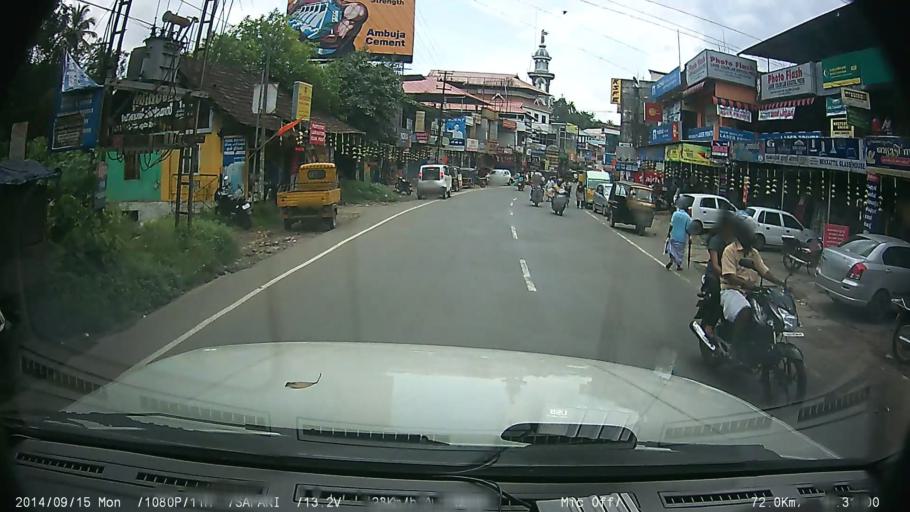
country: IN
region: Kerala
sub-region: Ernakulam
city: Piravam
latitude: 9.8604
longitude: 76.5943
